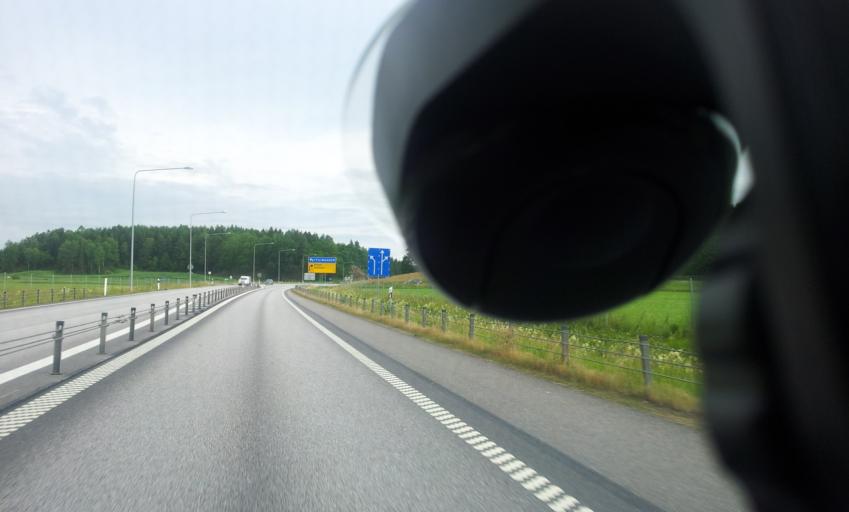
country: SE
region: OEstergoetland
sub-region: Valdemarsviks Kommun
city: Gusum
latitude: 58.3807
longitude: 16.4194
